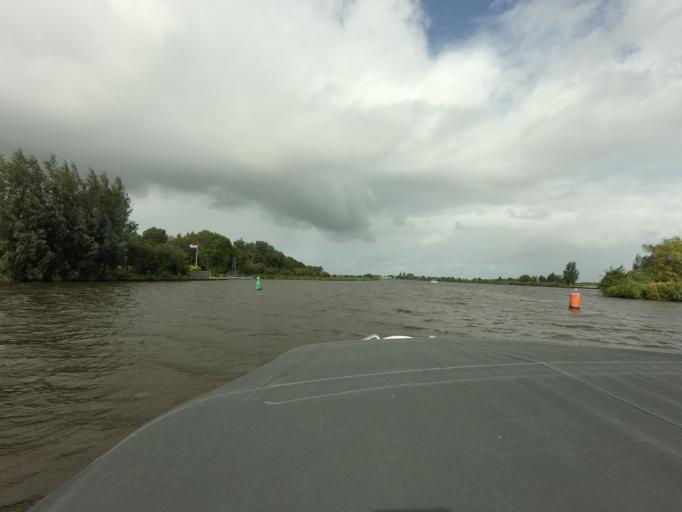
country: NL
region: Friesland
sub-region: Gemeente Boarnsterhim
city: Warten
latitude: 53.1388
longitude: 5.9144
